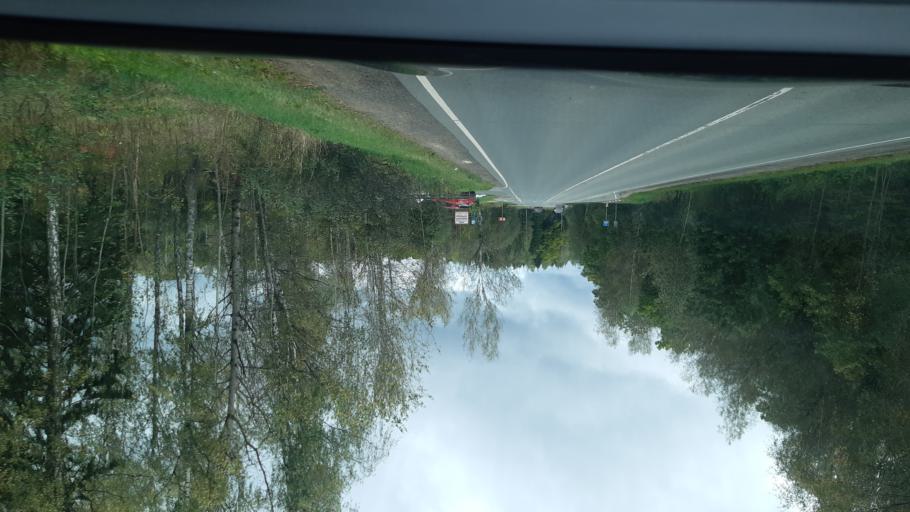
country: RU
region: Moskovskaya
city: Melikhovo
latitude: 55.1203
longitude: 37.6306
